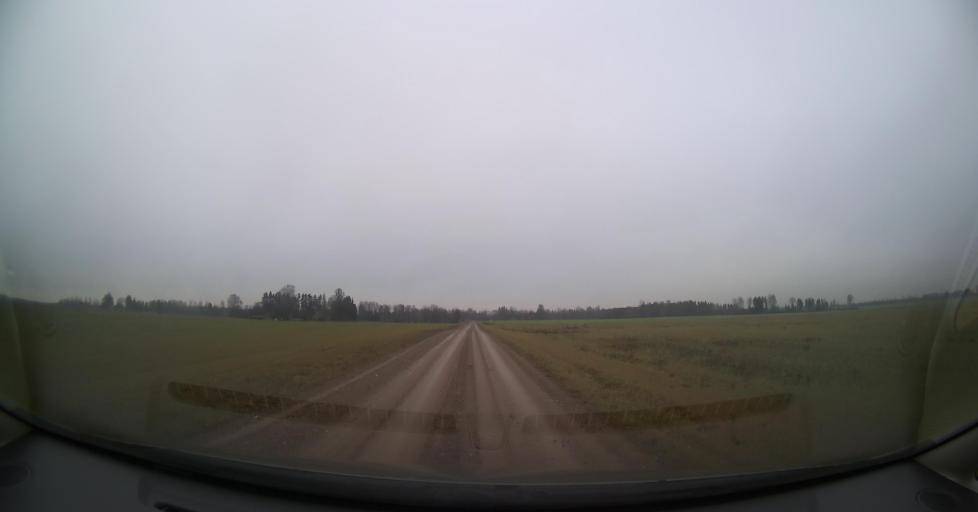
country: EE
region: Tartu
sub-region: Tartu linn
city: Tartu
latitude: 58.3869
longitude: 26.9276
